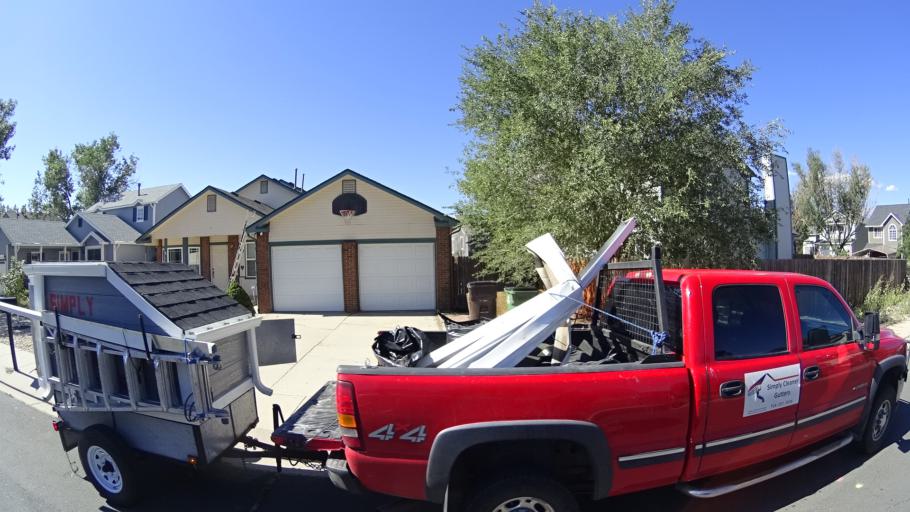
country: US
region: Colorado
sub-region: El Paso County
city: Stratmoor
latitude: 38.8130
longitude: -104.7413
